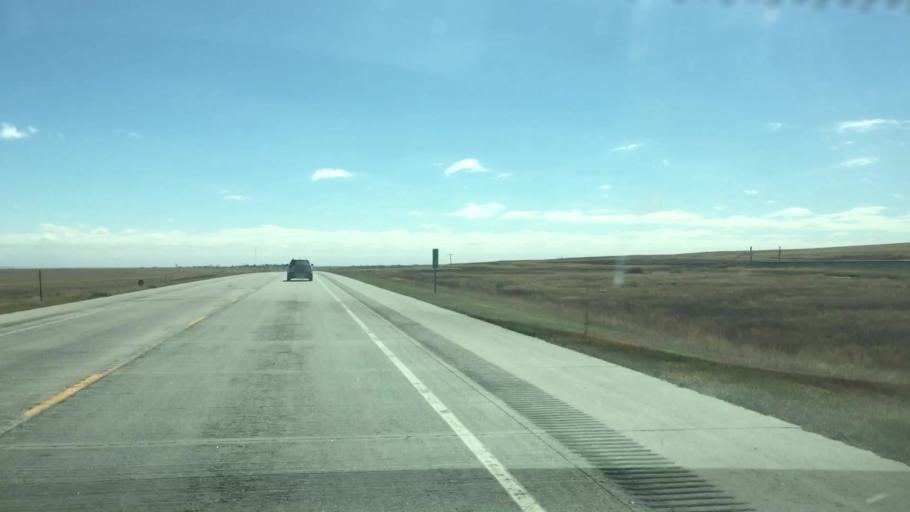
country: US
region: Colorado
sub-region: Lincoln County
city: Hugo
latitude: 39.1706
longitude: -103.5317
